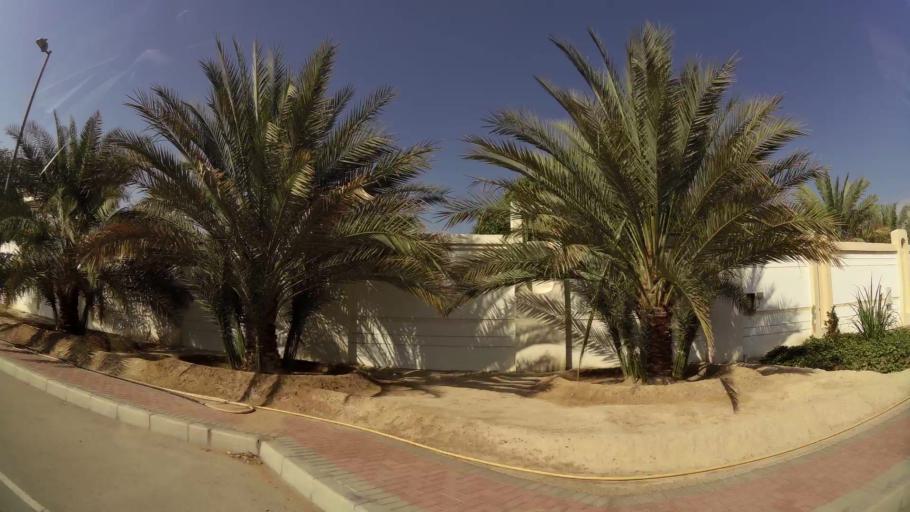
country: AE
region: Abu Dhabi
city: Al Ain
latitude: 24.0866
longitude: 55.9321
